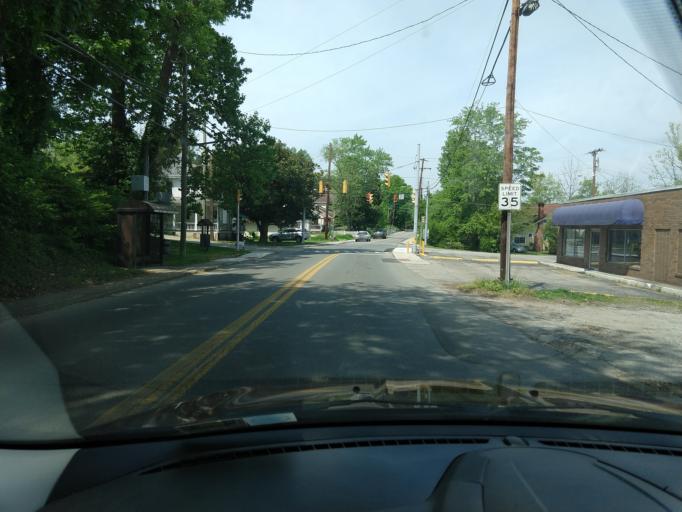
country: US
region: West Virginia
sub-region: Kanawha County
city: Saint Albans
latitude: 38.3811
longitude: -81.8251
